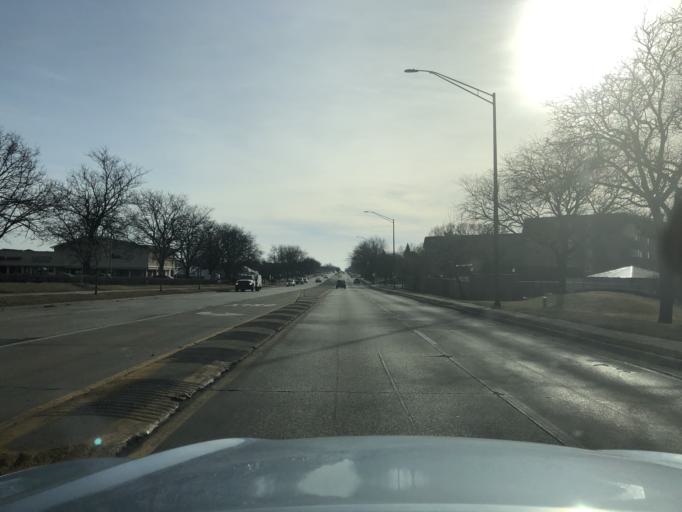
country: US
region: Illinois
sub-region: Cook County
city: Schaumburg
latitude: 42.0229
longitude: -88.0800
